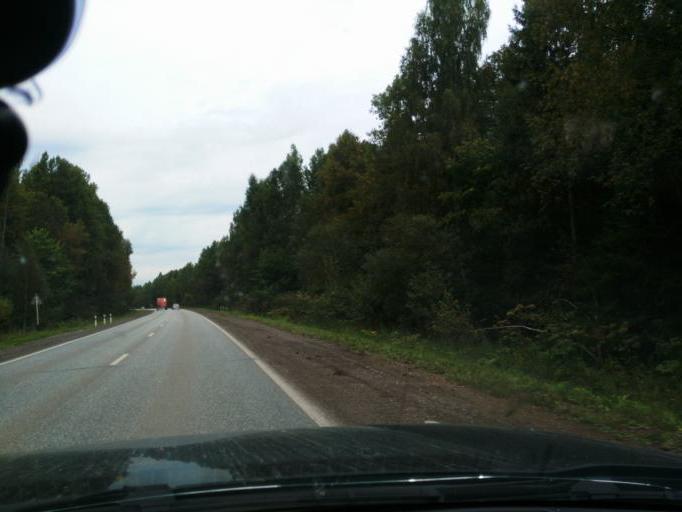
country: RU
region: Perm
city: Chernushka
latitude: 56.5965
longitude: 56.1592
